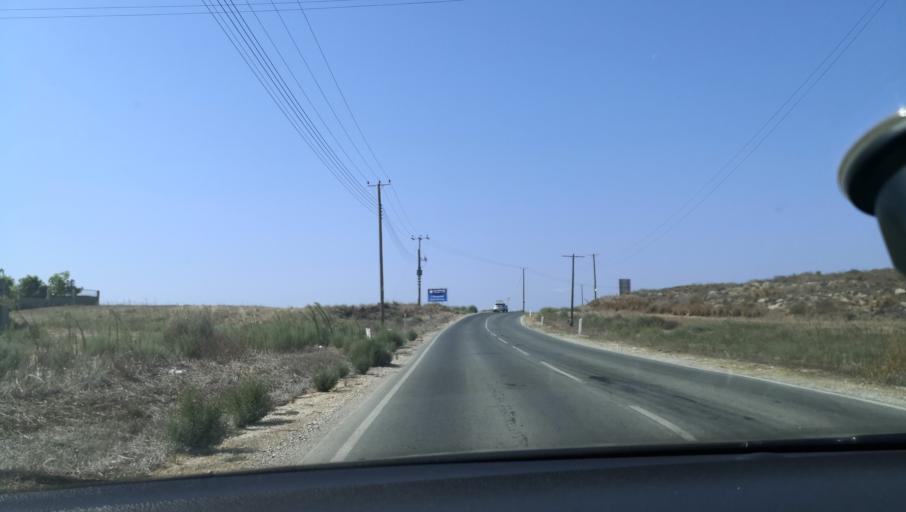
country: CY
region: Lefkosia
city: Kato Deftera
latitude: 35.1205
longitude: 33.2652
